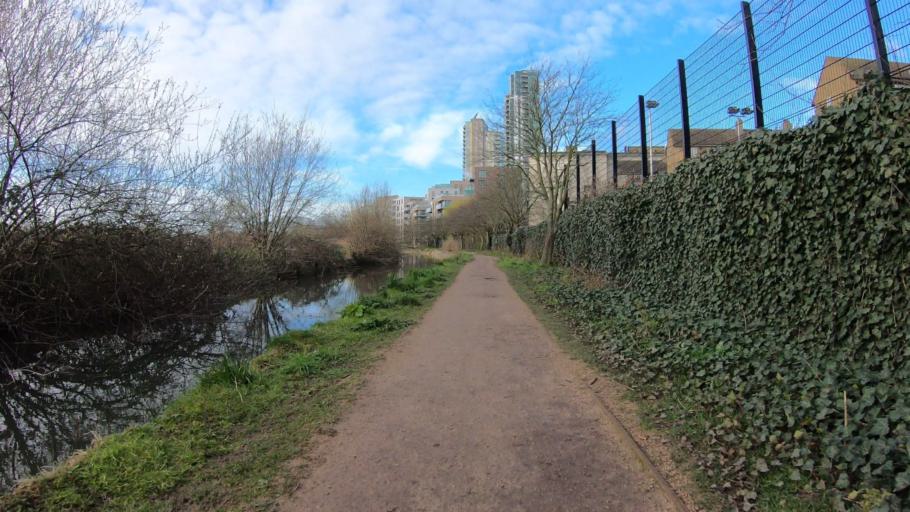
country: GB
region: England
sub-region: Greater London
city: Harringay
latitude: 51.5745
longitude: -0.0780
